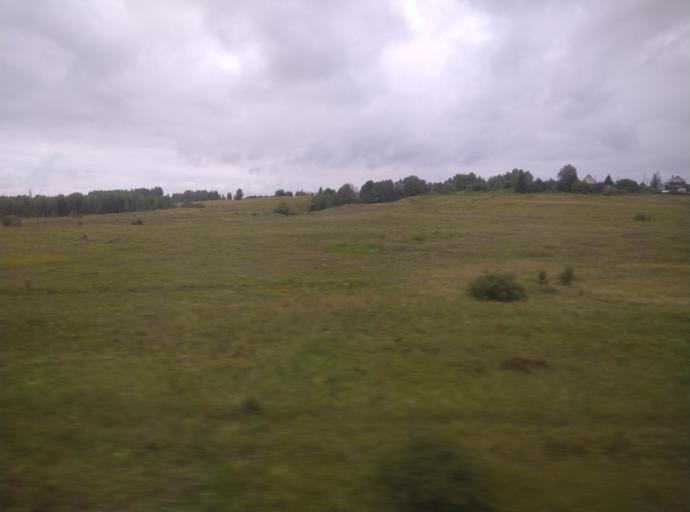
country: RU
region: Kostroma
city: Nerekhta
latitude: 57.4889
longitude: 40.6076
